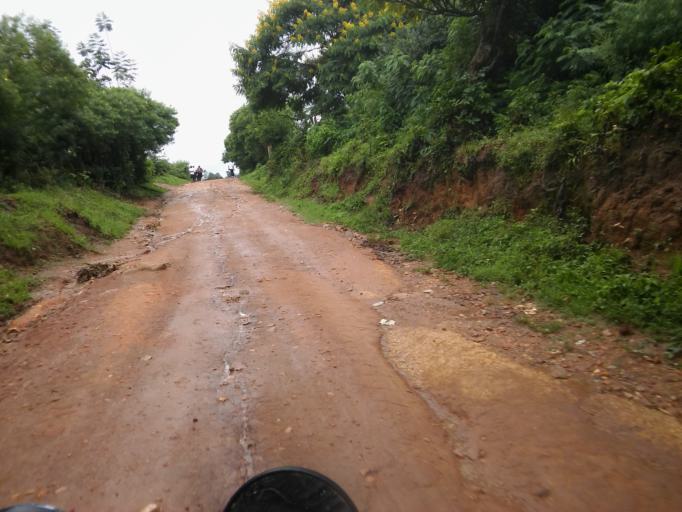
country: UG
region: Eastern Region
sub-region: Mbale District
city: Mbale
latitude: 0.9856
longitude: 34.2180
